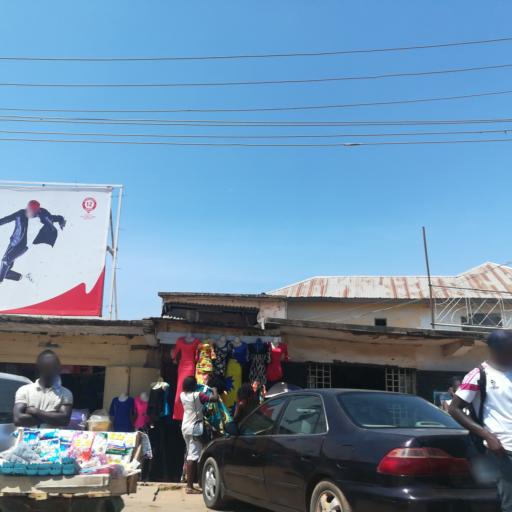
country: NG
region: Plateau
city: Bukuru
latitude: 9.7909
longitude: 8.8645
